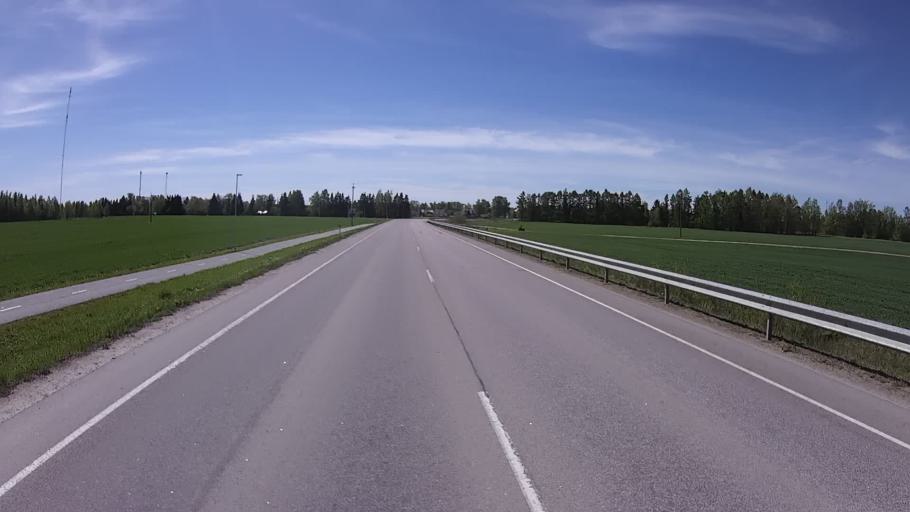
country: EE
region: Polvamaa
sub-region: Polva linn
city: Polva
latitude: 58.0751
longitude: 27.0883
